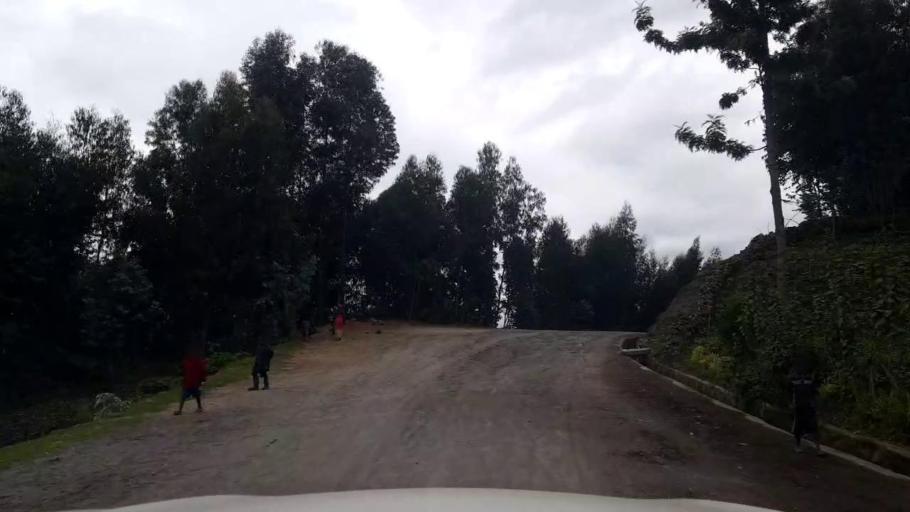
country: RW
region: Northern Province
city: Musanze
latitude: -1.5215
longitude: 29.5342
